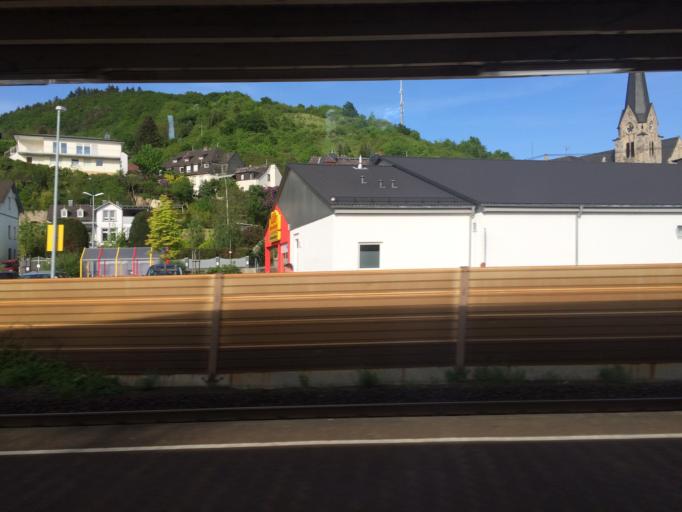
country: DE
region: Rheinland-Pfalz
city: Braubach
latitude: 50.2749
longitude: 7.6429
